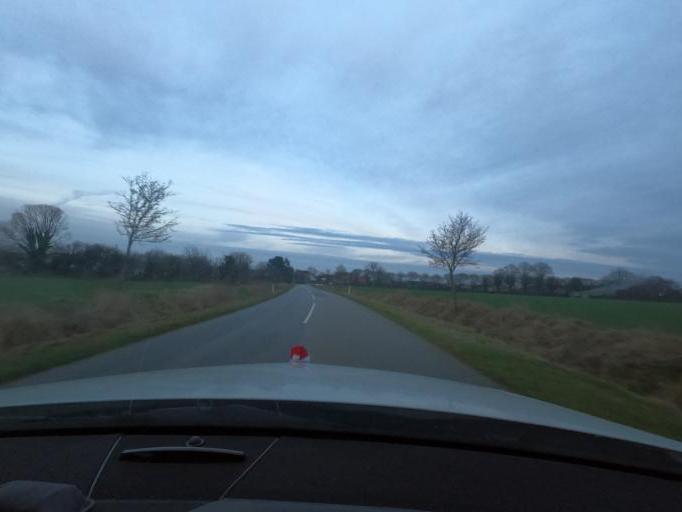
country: DK
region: South Denmark
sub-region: Sonderborg Kommune
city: Broager
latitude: 54.8586
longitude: 9.7202
